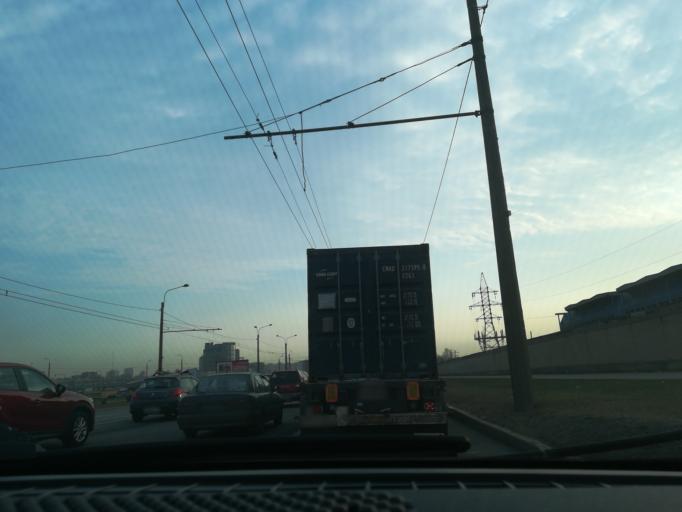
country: RU
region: St.-Petersburg
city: Avtovo
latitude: 59.8707
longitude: 30.2489
